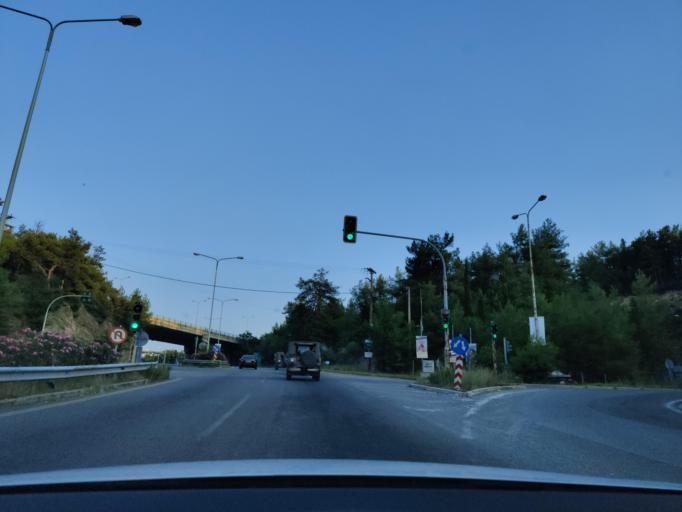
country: GR
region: East Macedonia and Thrace
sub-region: Nomos Kavalas
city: Amygdaleonas
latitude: 40.9438
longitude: 24.3739
